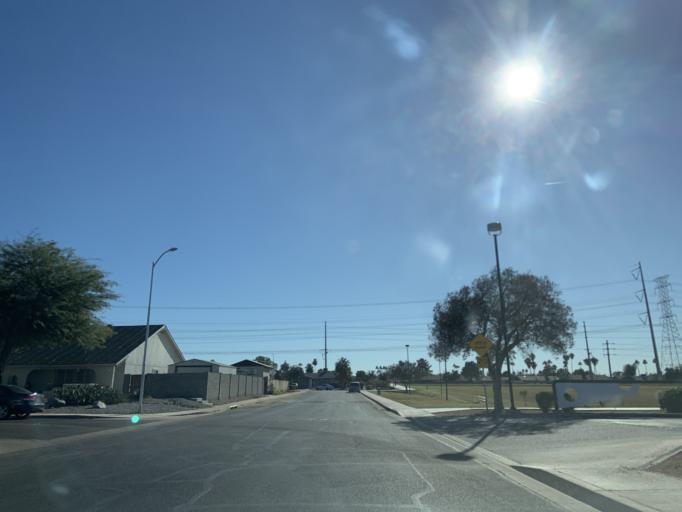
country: US
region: Arizona
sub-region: Maricopa County
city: San Carlos
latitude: 33.3585
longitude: -111.8725
